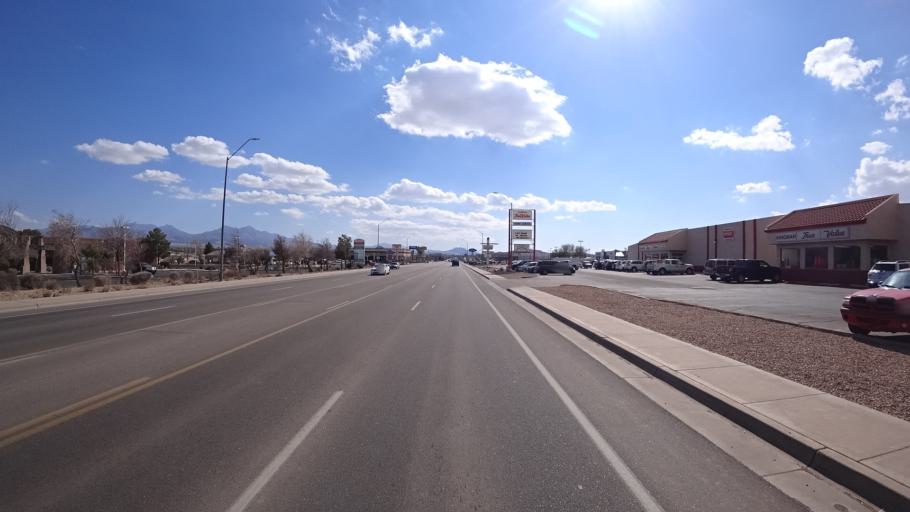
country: US
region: Arizona
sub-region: Mohave County
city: New Kingman-Butler
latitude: 35.2294
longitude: -114.0368
